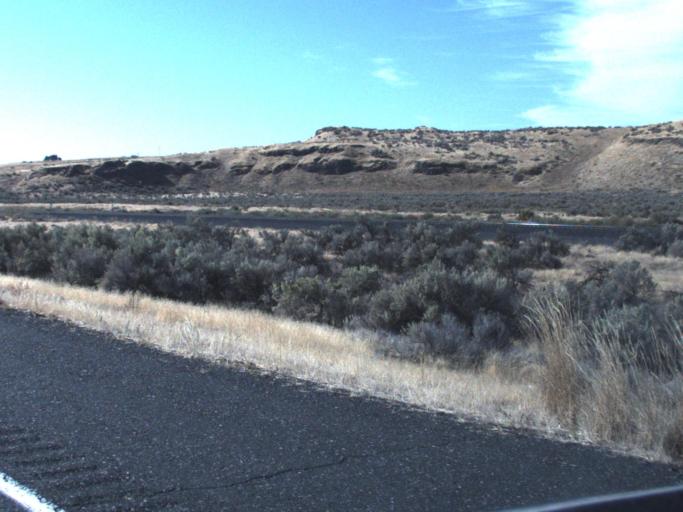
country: US
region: Washington
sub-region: Franklin County
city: Basin City
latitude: 46.4675
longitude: -119.0124
